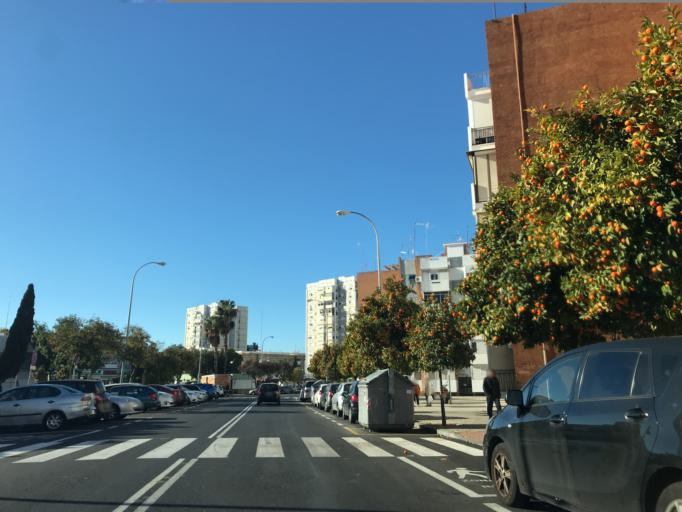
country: ES
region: Andalusia
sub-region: Provincia de Sevilla
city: Sevilla
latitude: 37.3995
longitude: -5.9583
